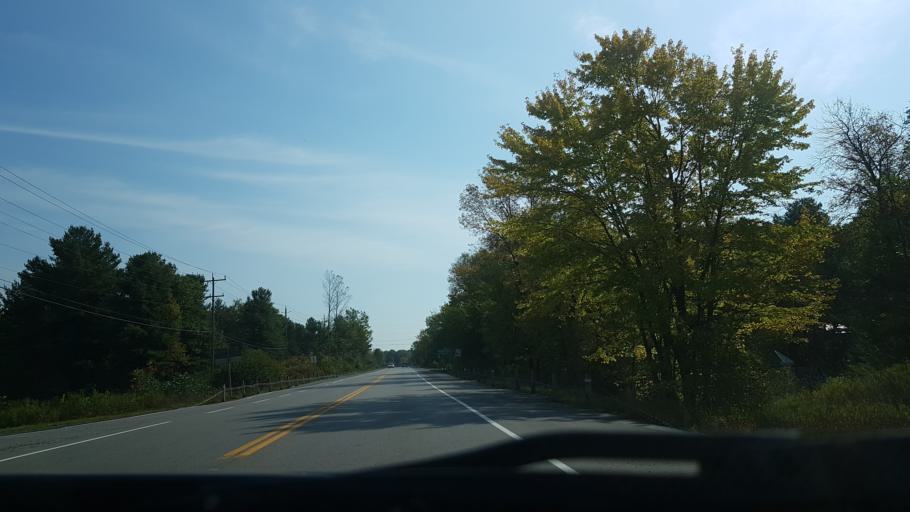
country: CA
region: Ontario
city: Orillia
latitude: 44.7458
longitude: -79.3226
